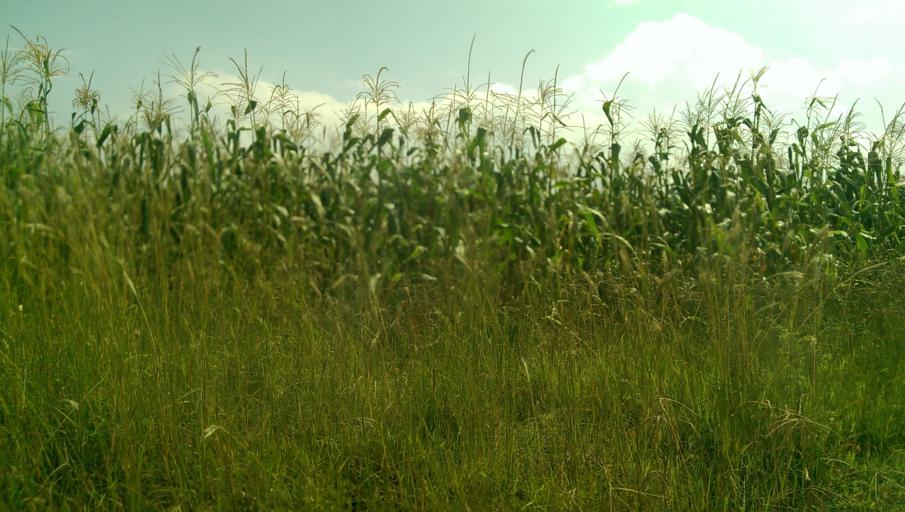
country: MX
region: Queretaro
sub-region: Huimilpan
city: San Jose Tepuzas
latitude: 20.3556
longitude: -100.3923
